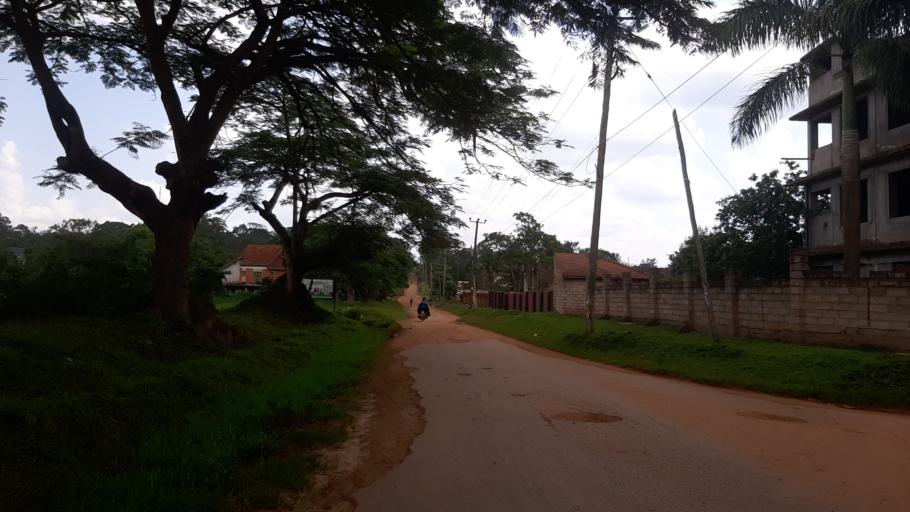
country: UG
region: Eastern Region
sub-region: Mbale District
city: Mbale
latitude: 1.0709
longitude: 34.1922
